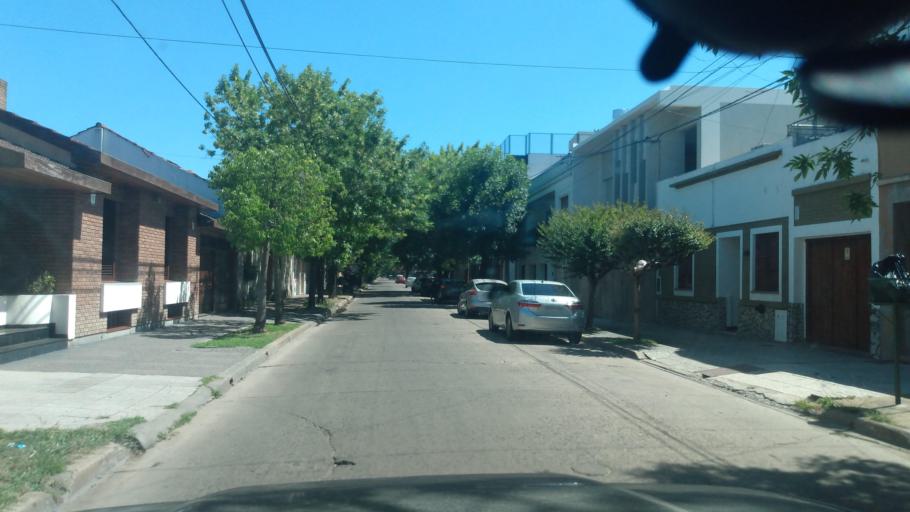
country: AR
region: Buenos Aires
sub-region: Partido de Lujan
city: Lujan
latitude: -34.5685
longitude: -59.1067
